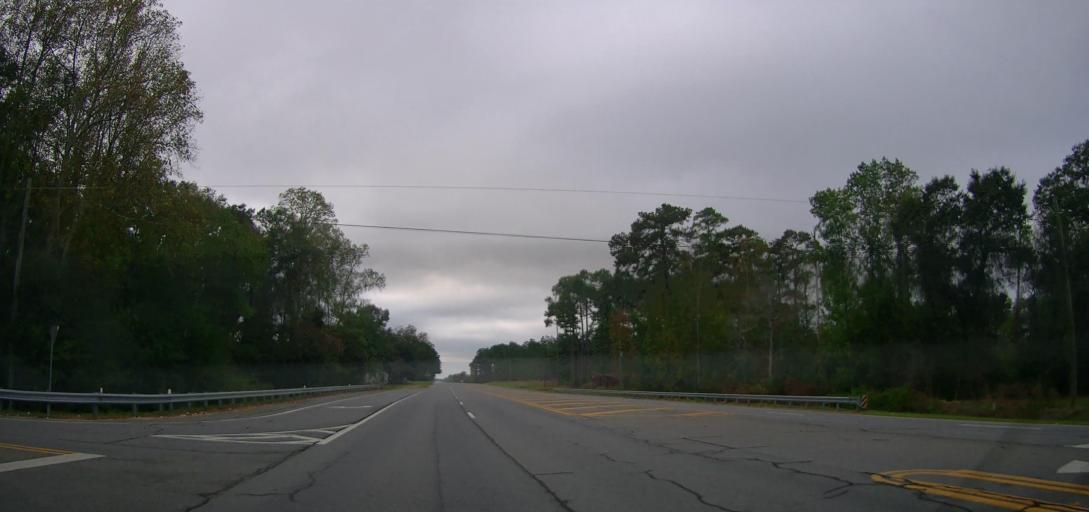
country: US
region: Georgia
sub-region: Tift County
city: Omega
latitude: 31.3020
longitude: -83.6479
